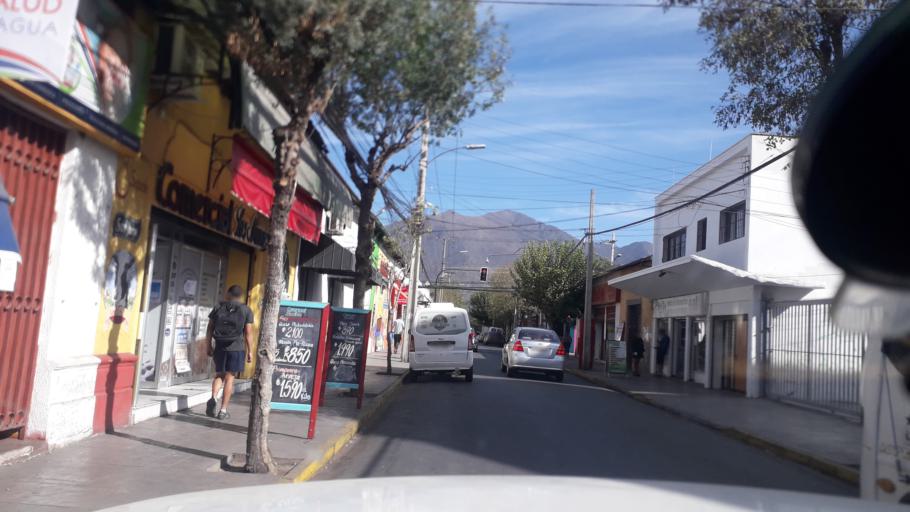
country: CL
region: Valparaiso
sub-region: Provincia de San Felipe
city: San Felipe
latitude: -32.7502
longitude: -70.7271
